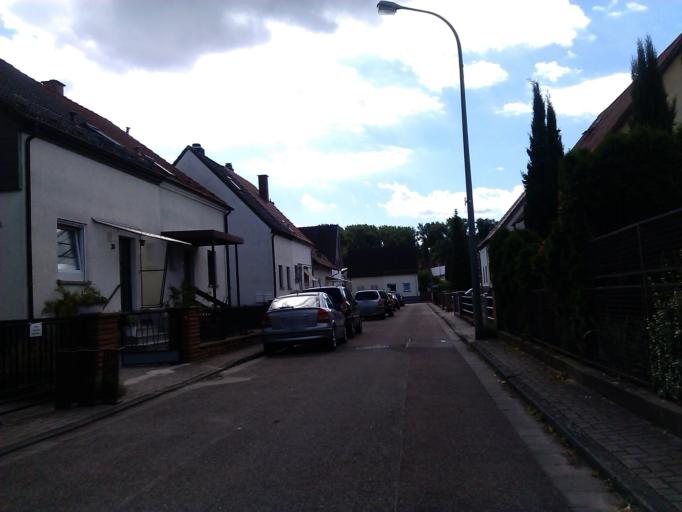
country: DE
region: Rheinland-Pfalz
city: Altrip
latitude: 49.4279
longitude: 8.4930
